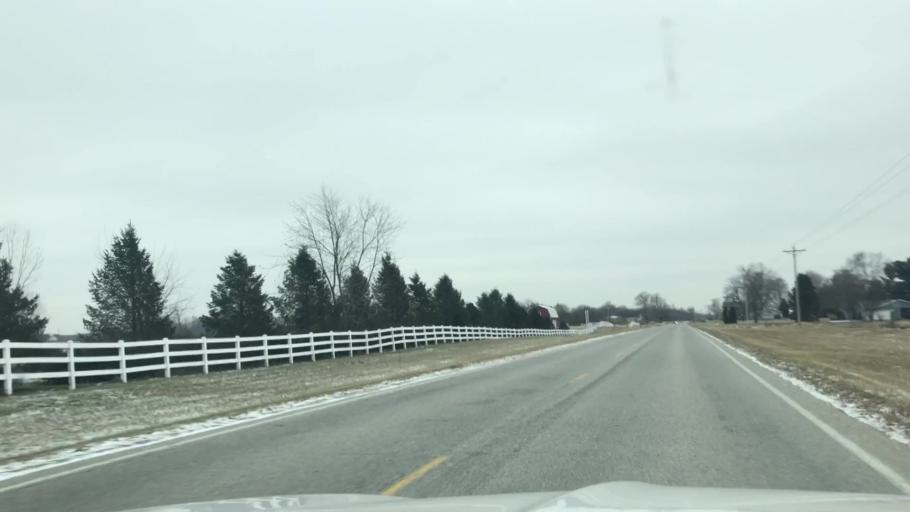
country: US
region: Indiana
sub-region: Fulton County
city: Rochester
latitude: 41.0357
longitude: -86.1995
